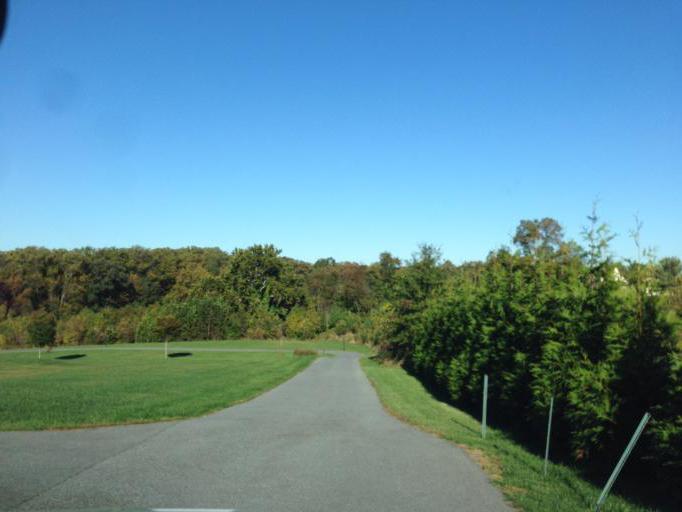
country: US
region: Maryland
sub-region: Howard County
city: Fulton
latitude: 39.1414
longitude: -76.9103
